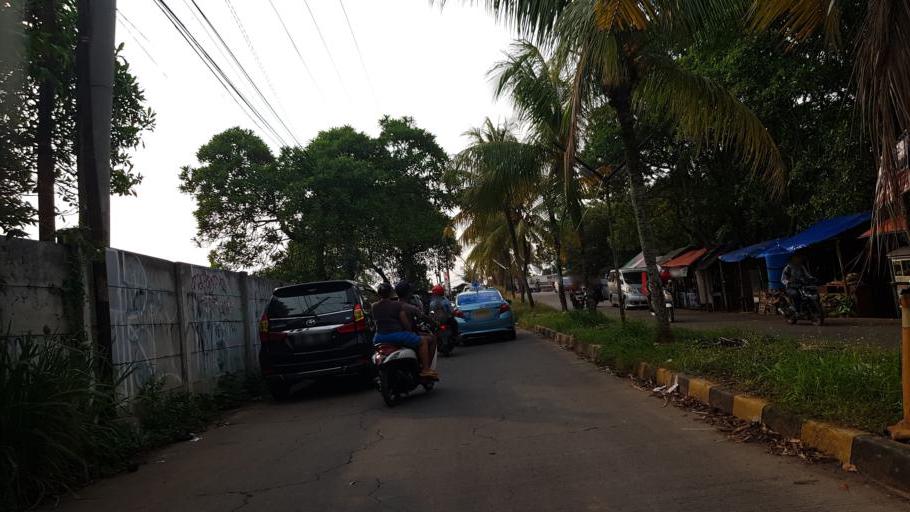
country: ID
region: West Java
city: Sawangan
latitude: -6.3723
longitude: 106.7918
